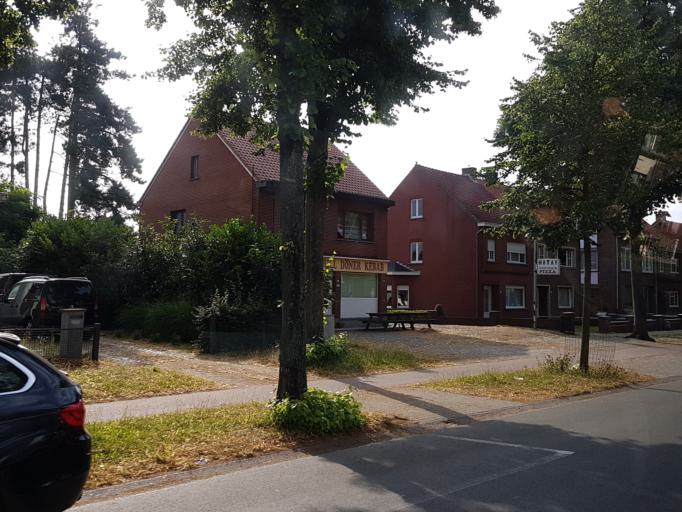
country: BE
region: Flanders
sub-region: Provincie Antwerpen
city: Westerlo
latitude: 51.0968
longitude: 4.9111
